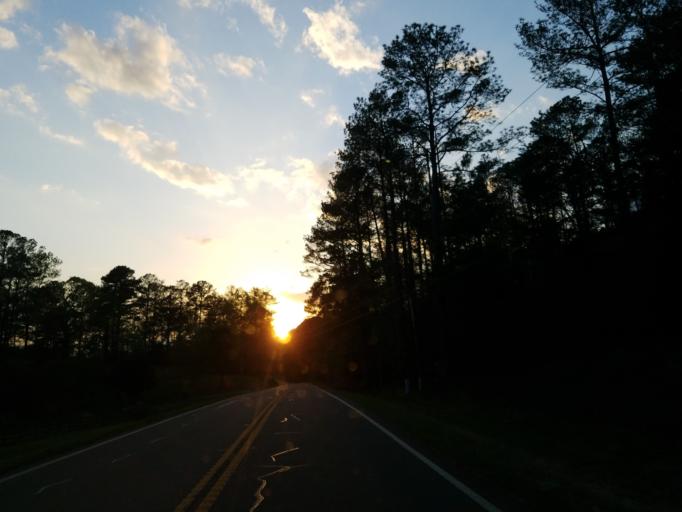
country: US
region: Georgia
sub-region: Pickens County
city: Jasper
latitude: 34.5123
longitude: -84.4467
